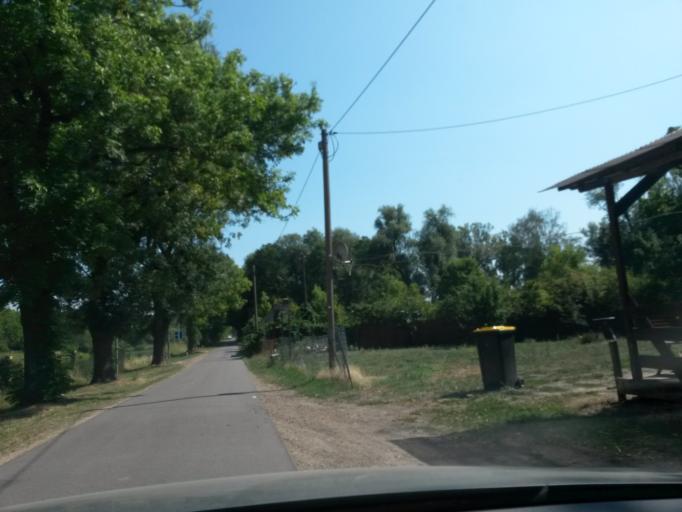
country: DE
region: Saxony-Anhalt
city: Jerichow
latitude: 52.4028
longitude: 11.9791
